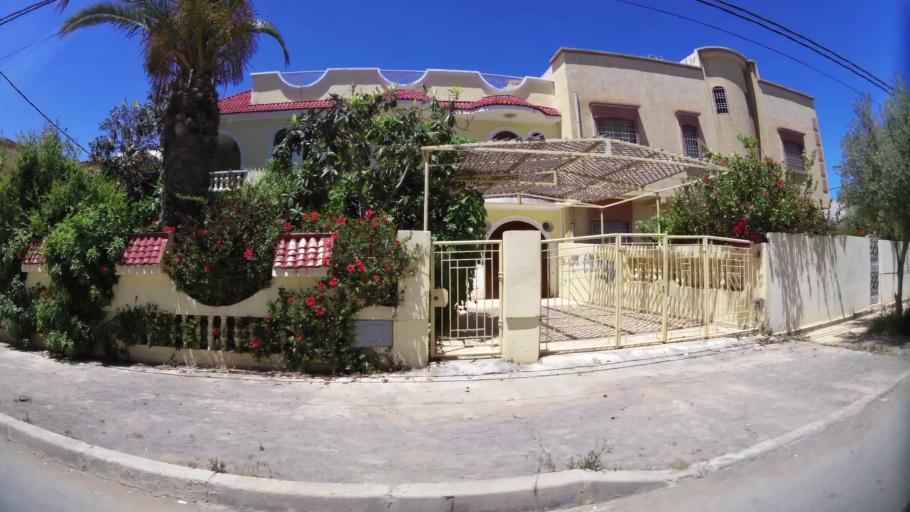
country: MA
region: Oriental
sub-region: Berkane-Taourirt
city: Madagh
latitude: 35.0847
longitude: -2.2324
